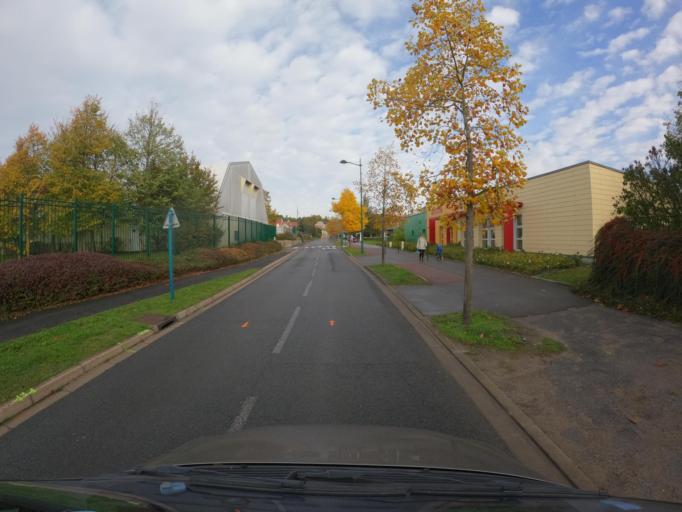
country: FR
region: Ile-de-France
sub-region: Departement de Seine-et-Marne
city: Courtry
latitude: 48.9150
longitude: 2.6040
